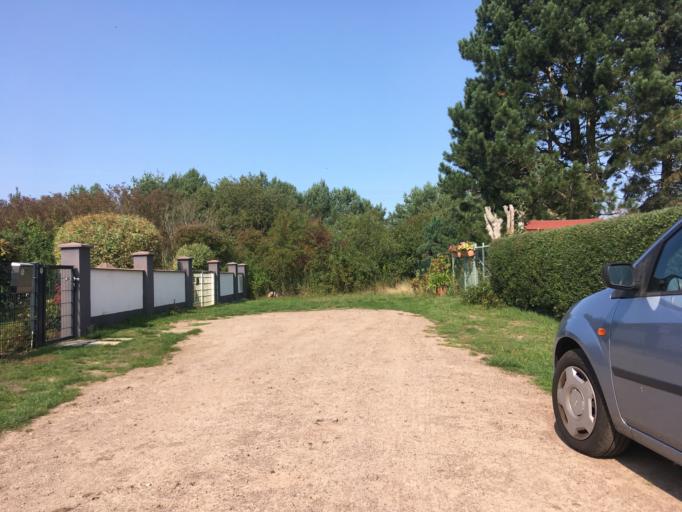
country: DE
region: Berlin
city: Falkenhagener Feld
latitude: 52.5874
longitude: 13.1361
